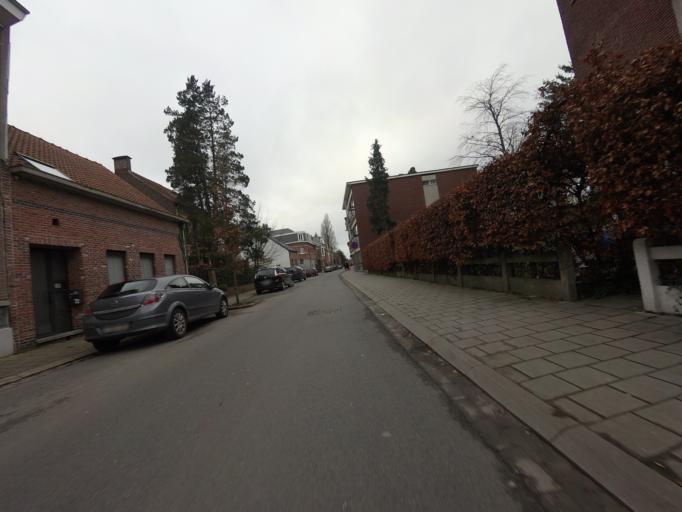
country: BE
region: Flanders
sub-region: Provincie Antwerpen
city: Hoboken
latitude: 51.1741
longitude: 4.3599
